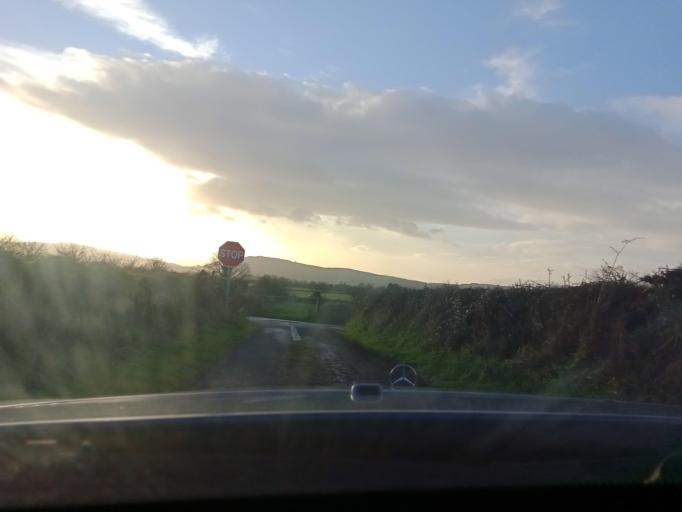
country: IE
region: Leinster
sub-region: Kilkenny
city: Callan
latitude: 52.4609
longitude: -7.4210
